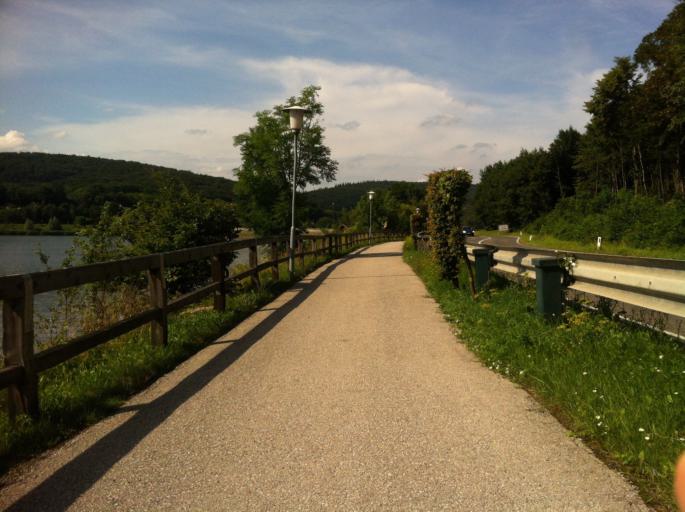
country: AT
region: Lower Austria
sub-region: Politischer Bezirk Wien-Umgebung
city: Wolfsgraben
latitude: 48.1797
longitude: 16.1226
